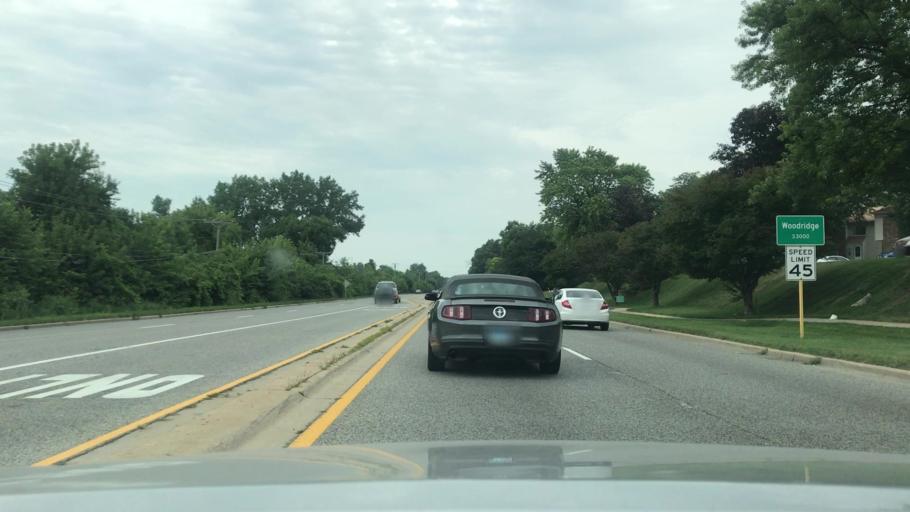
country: US
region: Illinois
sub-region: DuPage County
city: Woodridge
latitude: 41.7356
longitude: -88.0627
